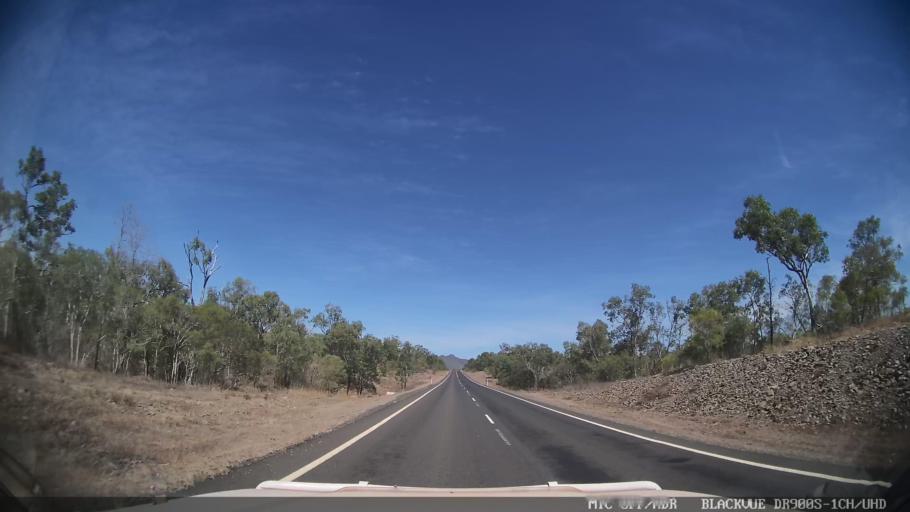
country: AU
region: Queensland
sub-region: Cook
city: Cooktown
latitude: -15.7015
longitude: 144.6067
